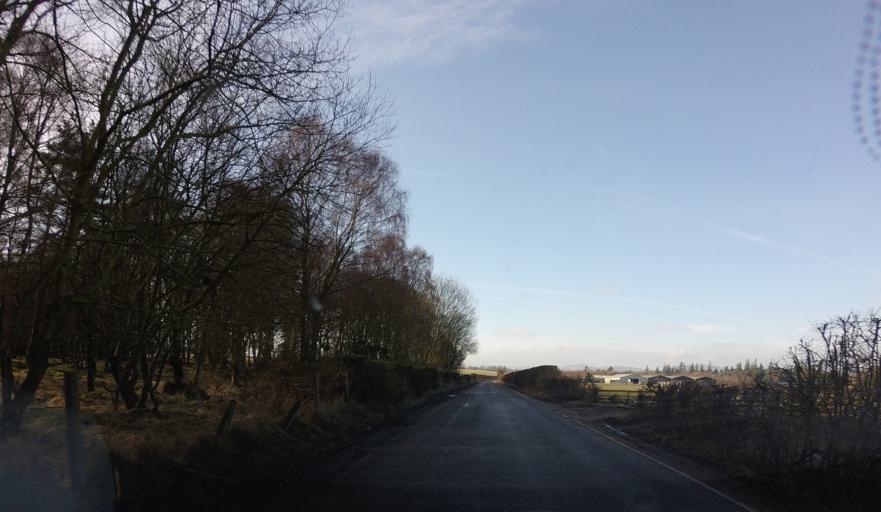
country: GB
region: Scotland
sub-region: Perth and Kinross
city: Stanley
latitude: 56.5256
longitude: -3.4368
